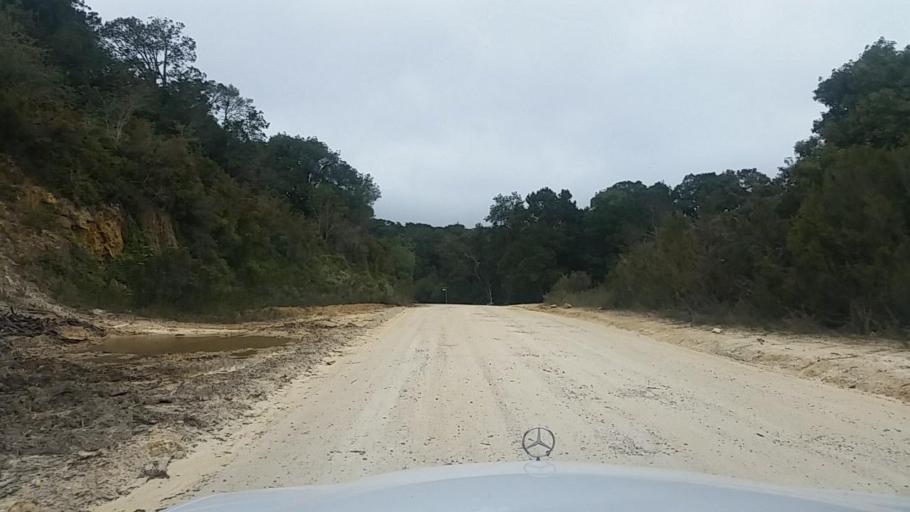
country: ZA
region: Western Cape
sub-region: Eden District Municipality
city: Knysna
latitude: -33.9553
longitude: 23.1534
